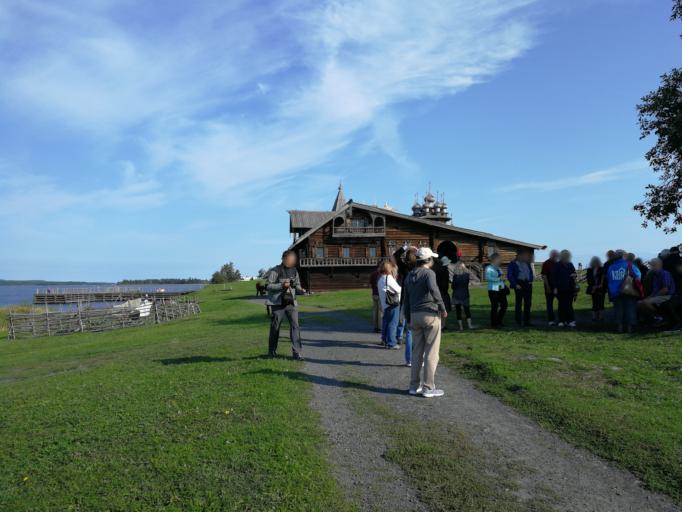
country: RU
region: Republic of Karelia
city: Shun'ga
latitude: 62.0660
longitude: 35.2235
